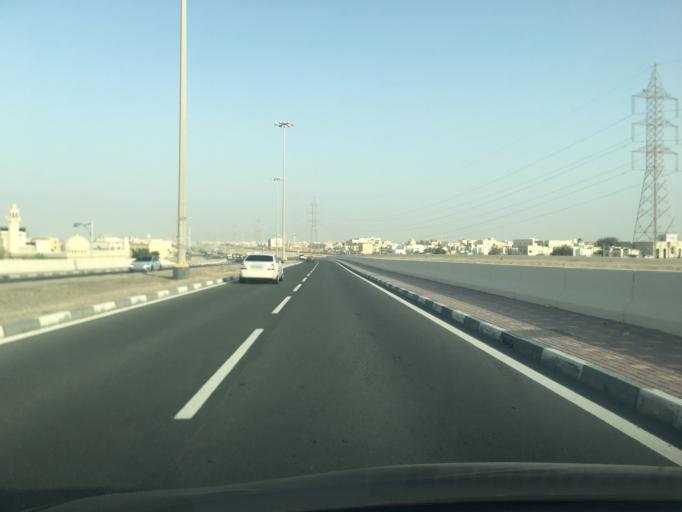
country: AE
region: Abu Dhabi
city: Abu Dhabi
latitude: 24.3262
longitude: 54.6234
